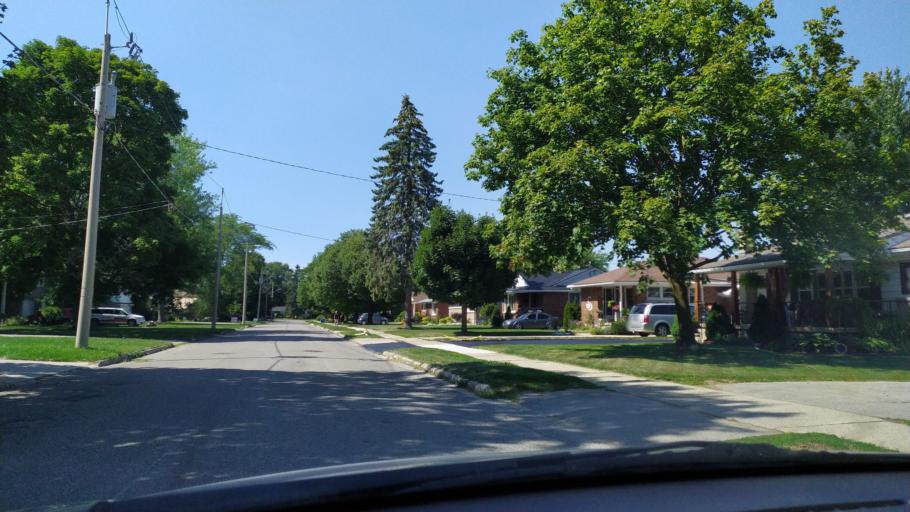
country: CA
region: Ontario
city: Stratford
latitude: 43.3650
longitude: -80.9969
